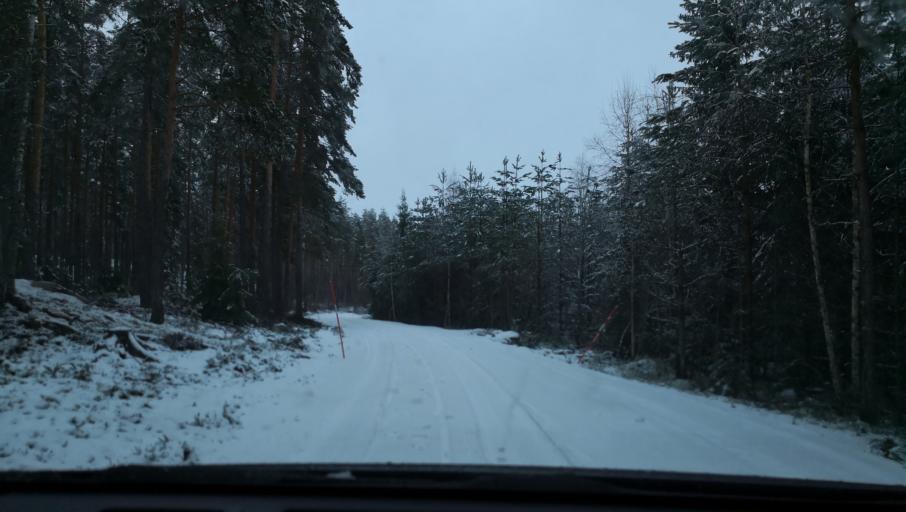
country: SE
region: Vaestmanland
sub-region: Kopings Kommun
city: Kolsva
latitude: 59.5671
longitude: 15.8188
